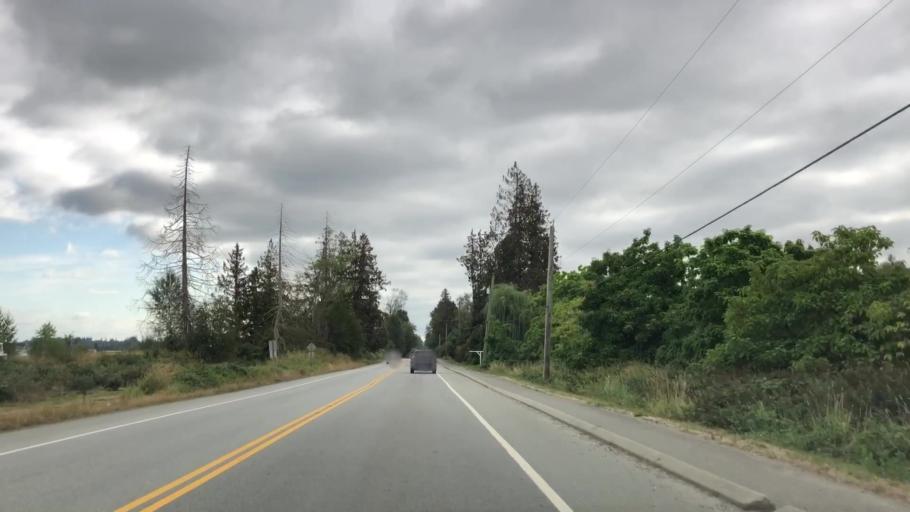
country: US
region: Washington
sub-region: Whatcom County
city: Blaine
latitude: 49.0601
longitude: -122.7450
